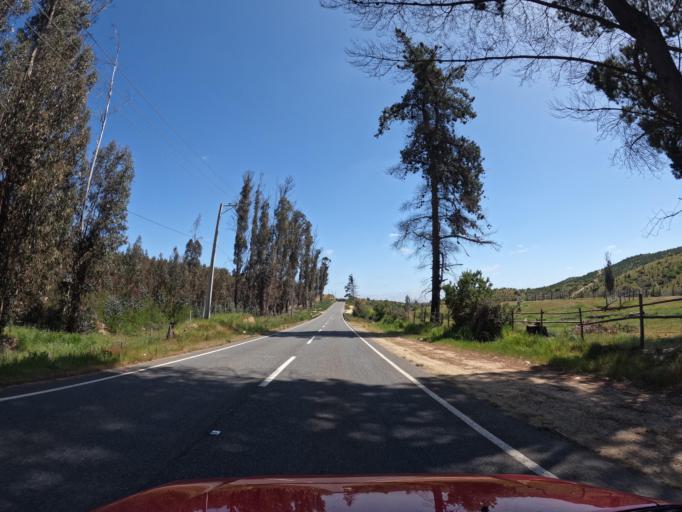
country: CL
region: O'Higgins
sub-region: Provincia de Colchagua
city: Santa Cruz
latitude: -34.6624
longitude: -71.8398
